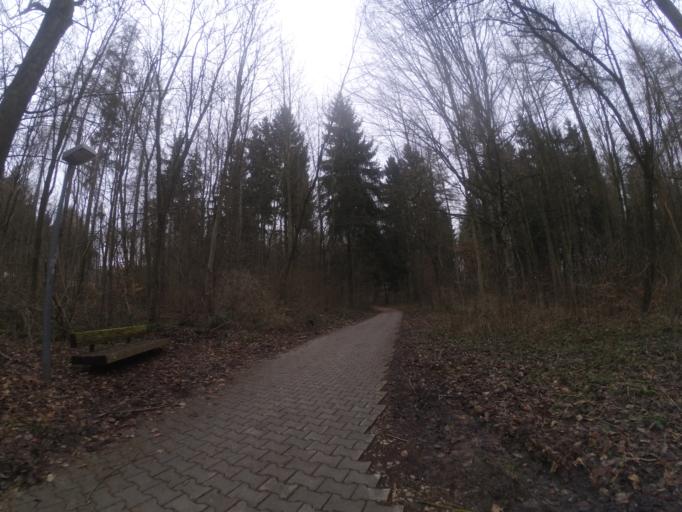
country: DE
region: Baden-Wuerttemberg
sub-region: Tuebingen Region
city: Ulm
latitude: 48.4174
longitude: 9.9640
